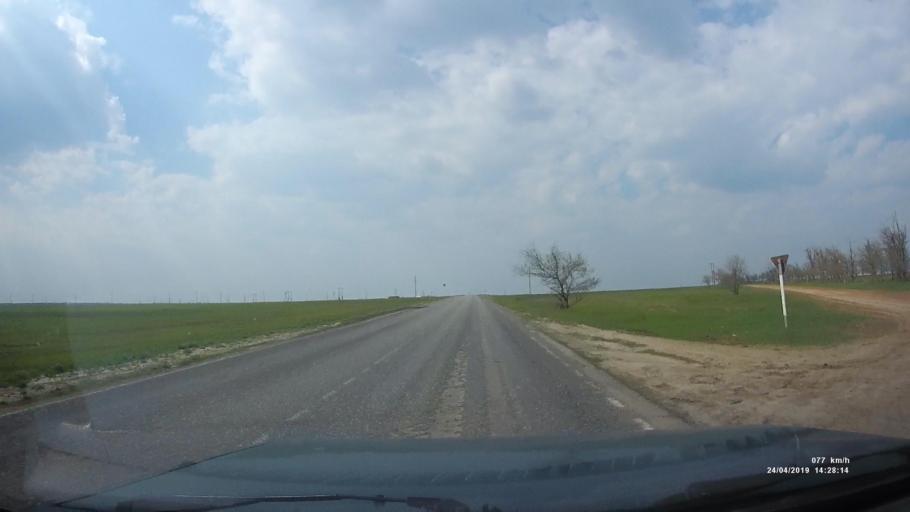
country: RU
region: Kalmykiya
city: Arshan'
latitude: 46.3374
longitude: 44.0324
